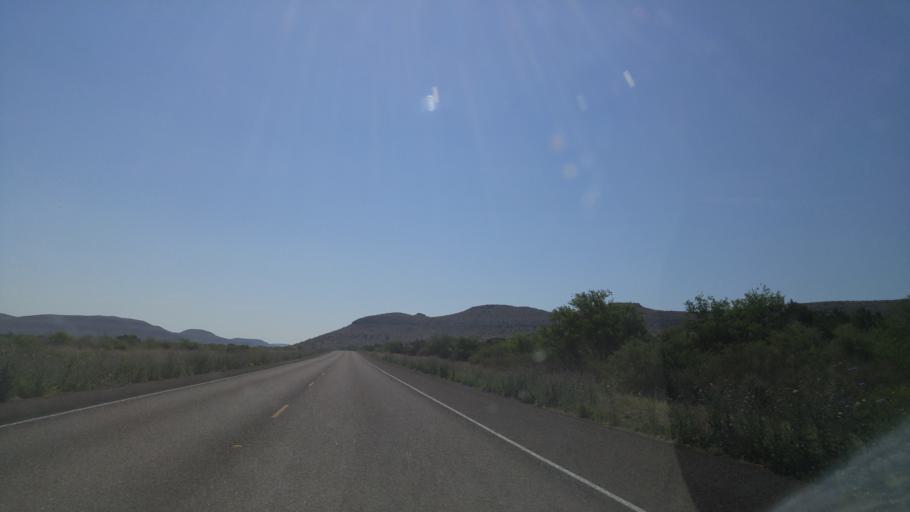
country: US
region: Texas
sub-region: Terrell County
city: Sanderson
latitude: 30.1748
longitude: -102.7491
